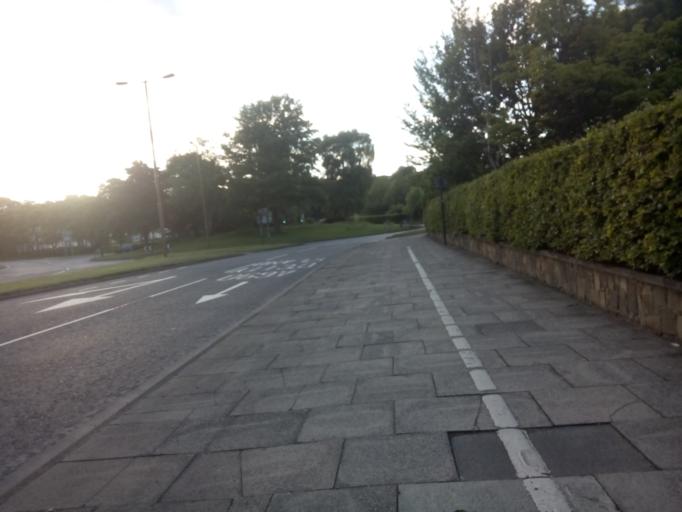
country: GB
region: England
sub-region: County Durham
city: Durham
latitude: 54.7844
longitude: -1.5859
